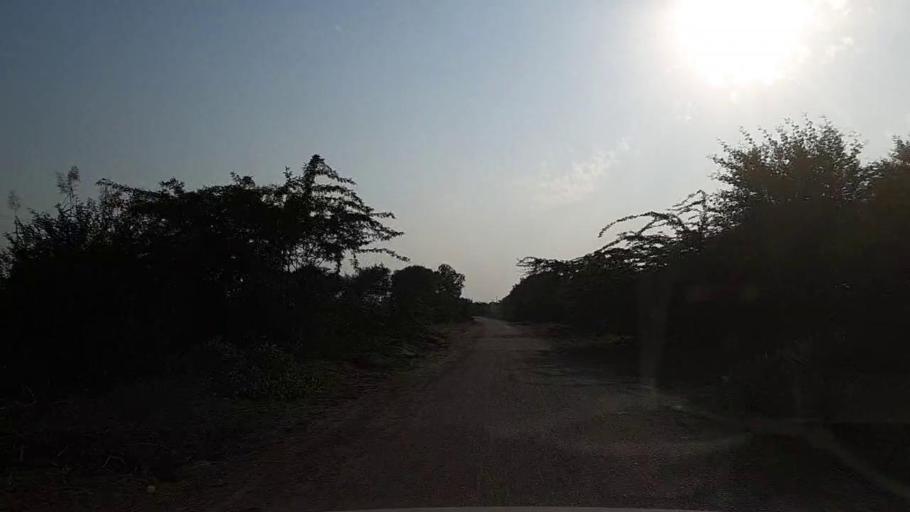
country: PK
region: Sindh
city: Mirpur Batoro
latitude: 24.7777
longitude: 68.2408
